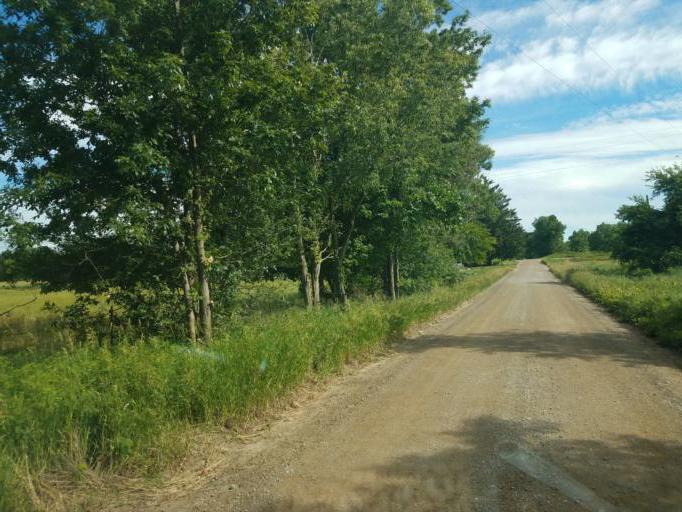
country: US
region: Michigan
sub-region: Barry County
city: Nashville
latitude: 42.5988
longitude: -84.9755
